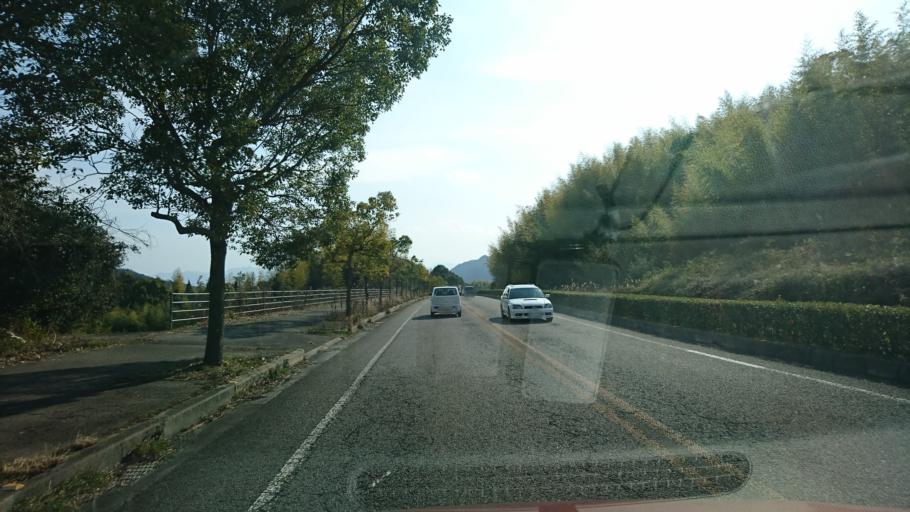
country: JP
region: Ehime
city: Saijo
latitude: 34.0139
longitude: 133.0332
